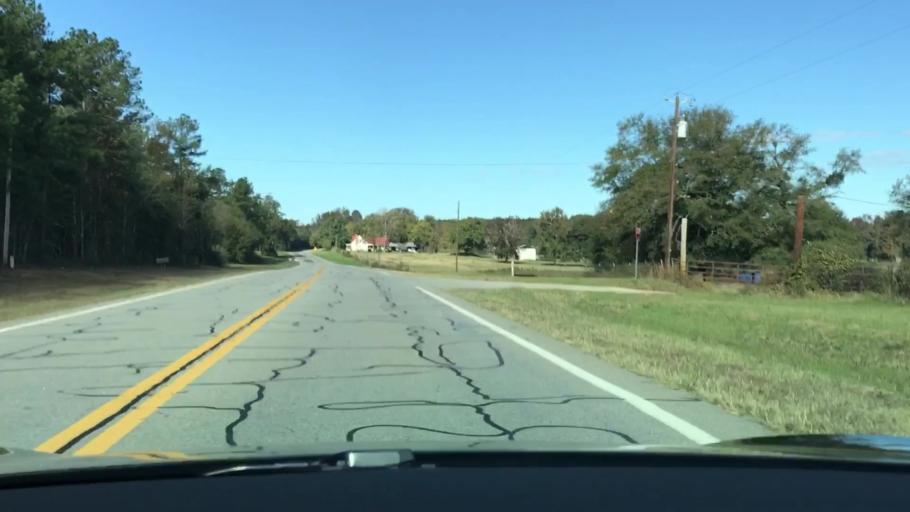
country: US
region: Georgia
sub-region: Warren County
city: Warrenton
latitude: 33.3429
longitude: -82.5765
